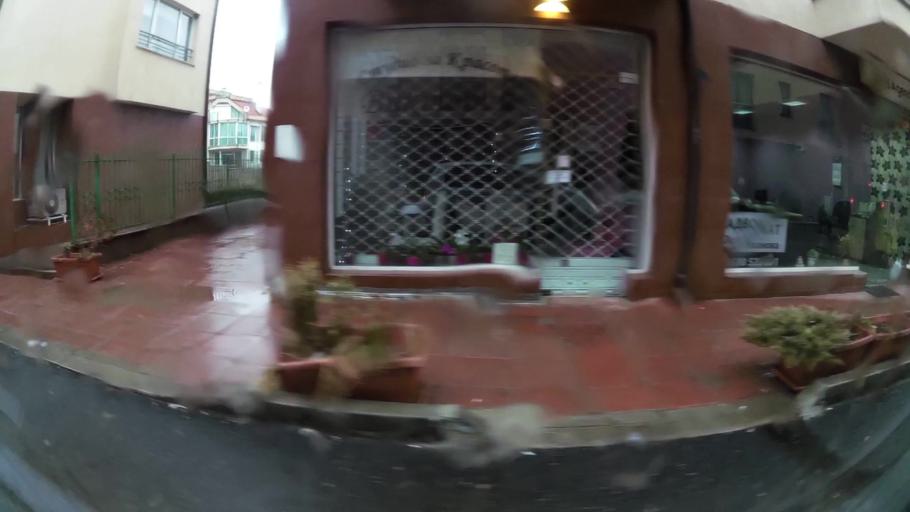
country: BG
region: Sofia-Capital
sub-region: Stolichna Obshtina
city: Sofia
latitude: 42.6431
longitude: 23.3323
